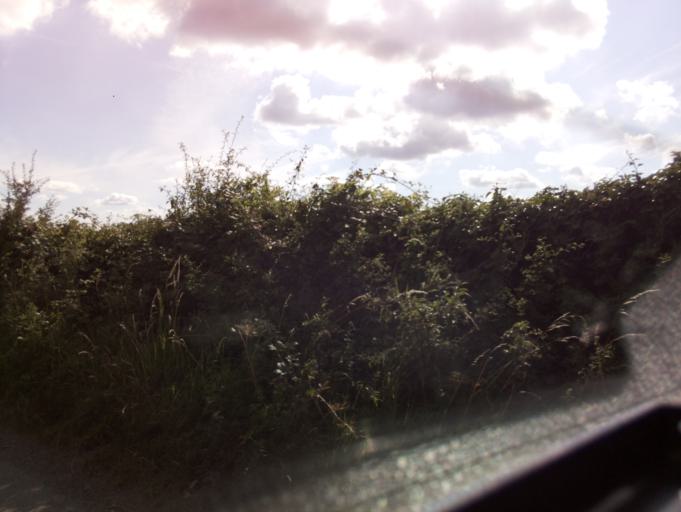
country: GB
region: England
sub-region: Gloucestershire
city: Coates
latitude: 51.7022
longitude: -2.0441
